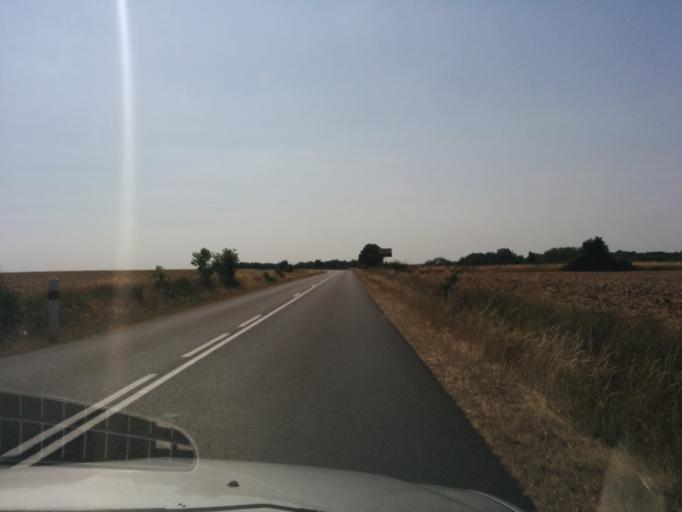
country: FR
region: Poitou-Charentes
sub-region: Departement de la Vienne
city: Moncontour
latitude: 46.8087
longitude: -0.0021
